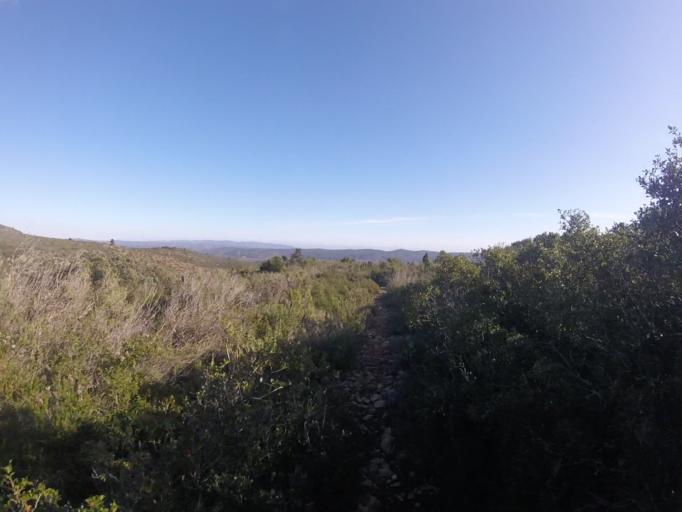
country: ES
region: Valencia
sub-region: Provincia de Castello
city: Sarratella
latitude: 40.2912
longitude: 0.0522
